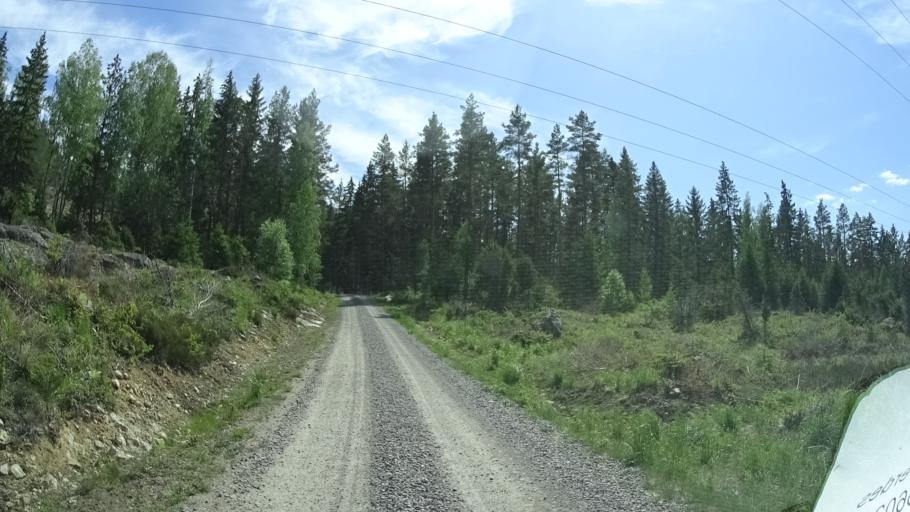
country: SE
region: OEstergoetland
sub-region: Norrkopings Kommun
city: Svartinge
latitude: 58.7731
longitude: 15.9287
